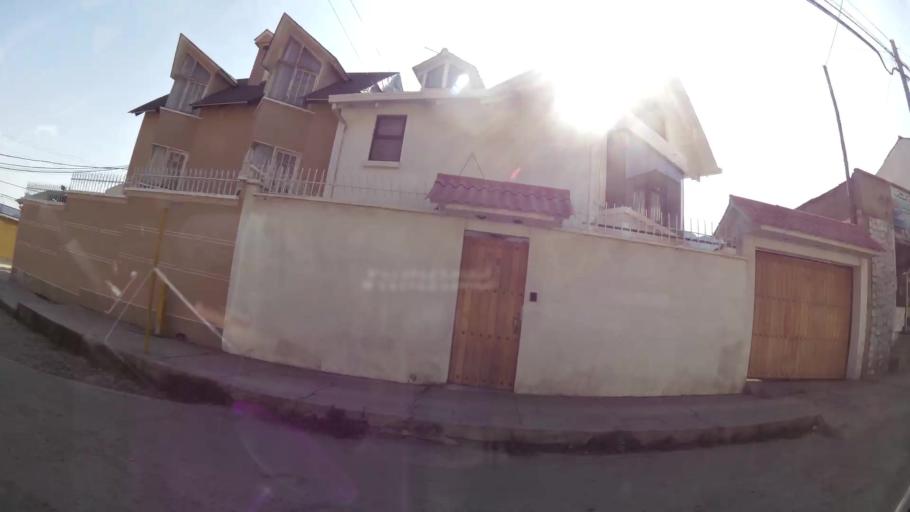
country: BO
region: La Paz
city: La Paz
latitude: -16.5183
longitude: -68.0625
